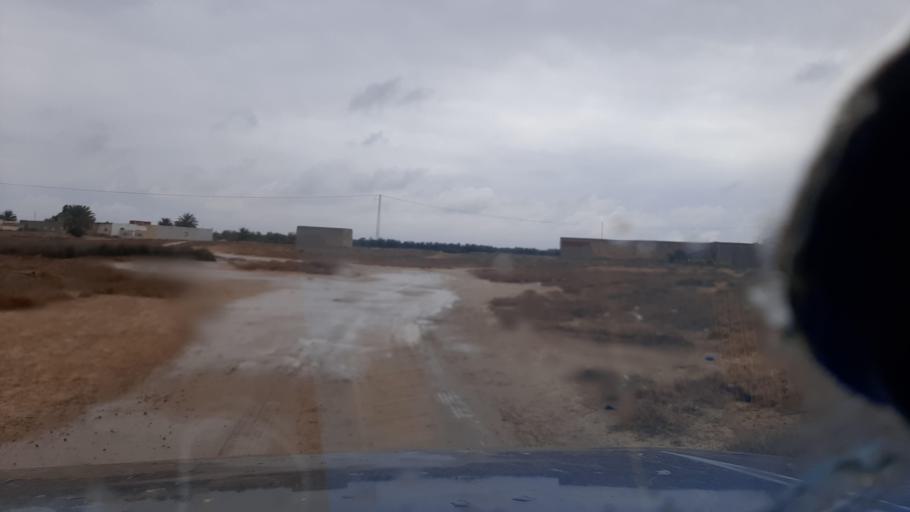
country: TN
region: Al Mahdiyah
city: Shurban
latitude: 35.4358
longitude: 10.4032
